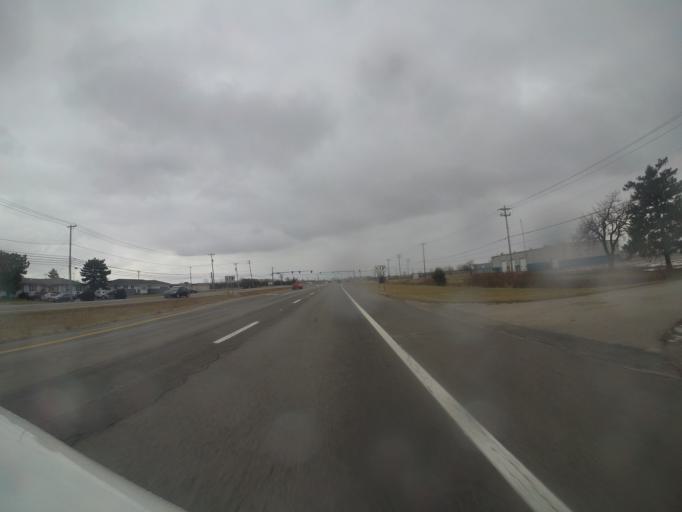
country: US
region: Ohio
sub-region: Wood County
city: Rossford
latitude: 41.5648
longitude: -83.5597
